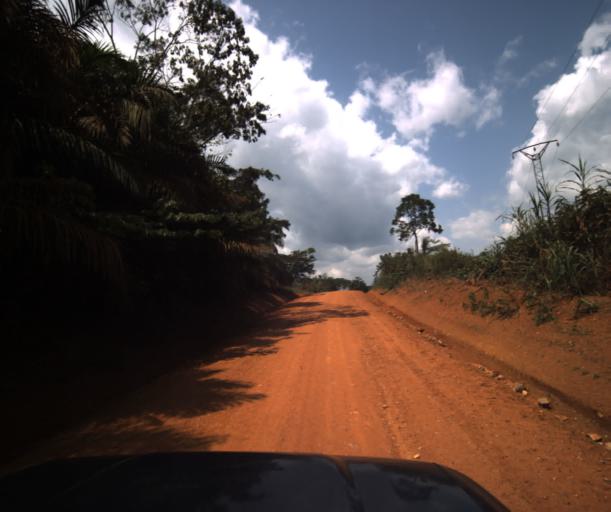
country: CM
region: Centre
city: Akono
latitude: 3.5535
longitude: 11.0587
